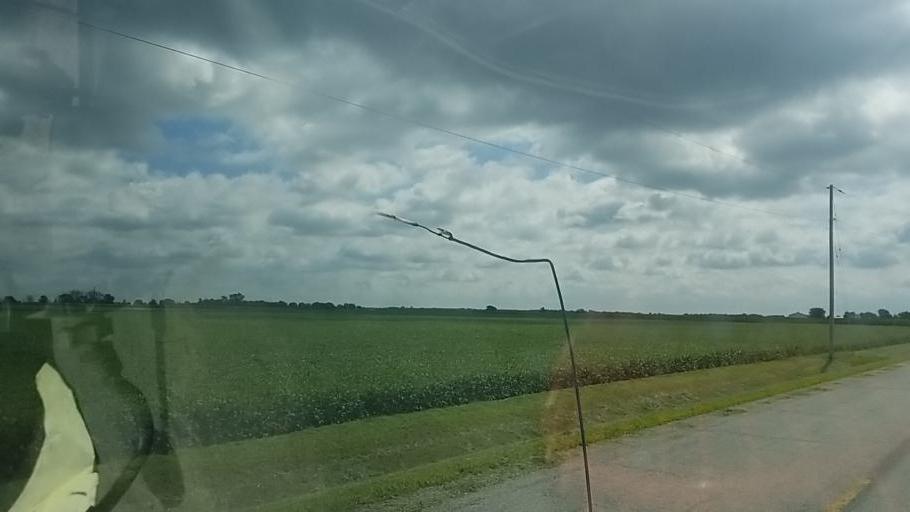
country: US
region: Ohio
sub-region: Madison County
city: Bethel
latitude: 39.7442
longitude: -83.3688
